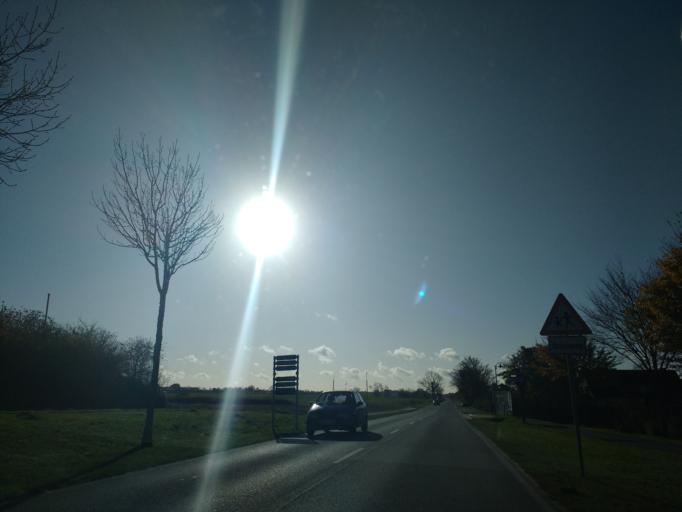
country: DE
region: Mecklenburg-Vorpommern
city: Ostseebad Boltenhagen
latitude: 53.9842
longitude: 11.1916
